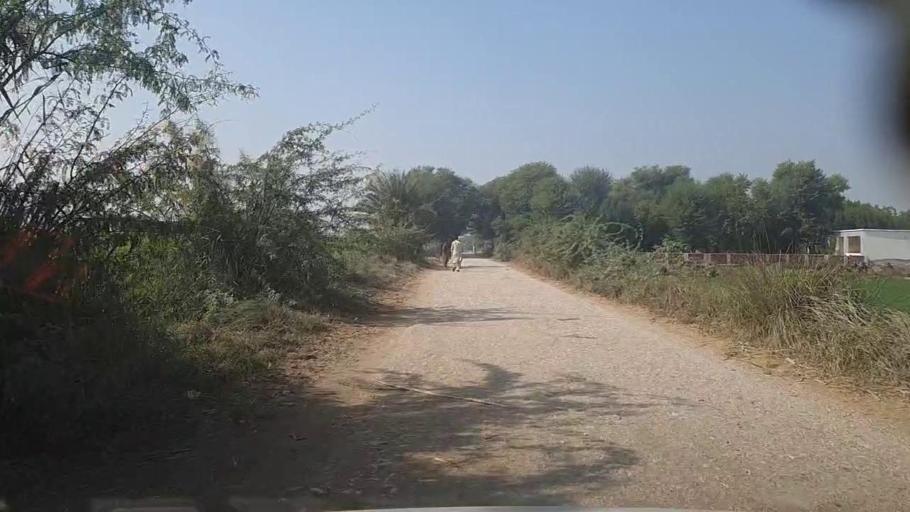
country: PK
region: Sindh
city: Karaundi
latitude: 26.9796
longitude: 68.4478
